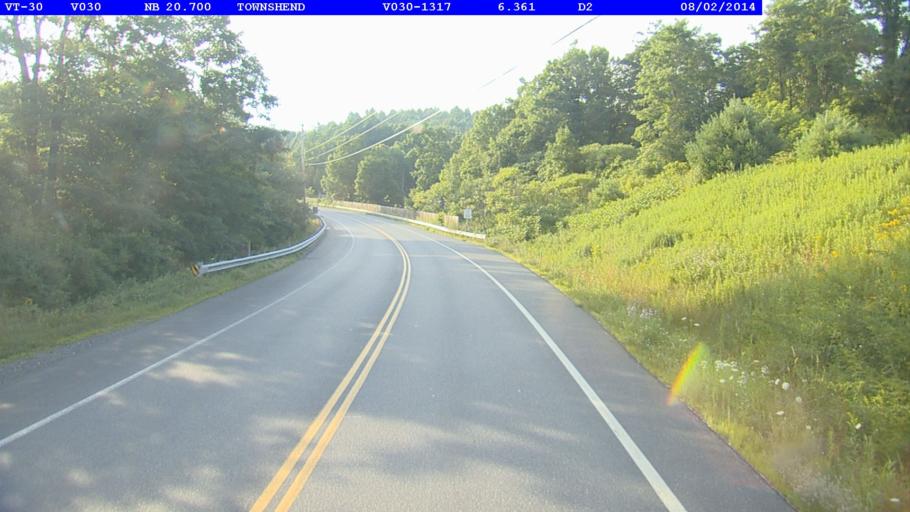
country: US
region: Vermont
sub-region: Windham County
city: Newfane
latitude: 43.0830
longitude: -72.7086
